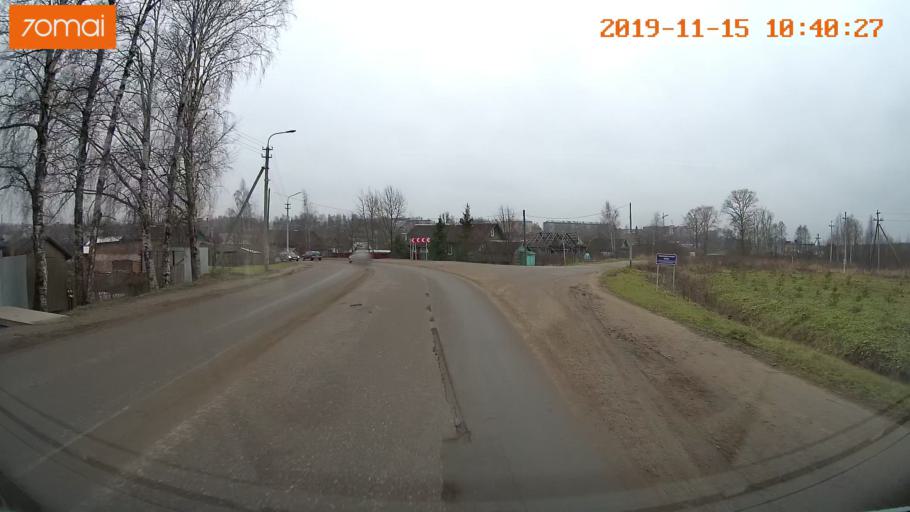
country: RU
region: Vologda
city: Sheksna
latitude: 59.2142
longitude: 38.5092
